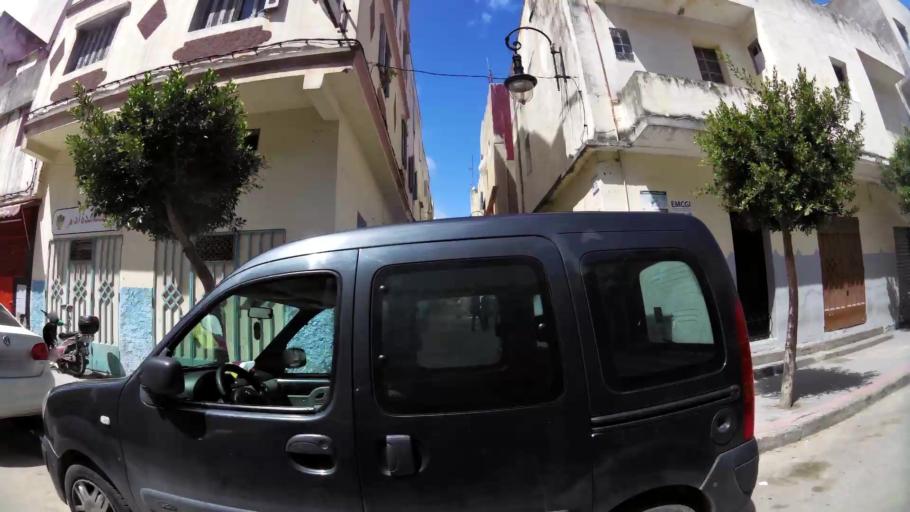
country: MA
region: Tanger-Tetouan
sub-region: Tanger-Assilah
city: Tangier
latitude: 35.7665
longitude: -5.8276
